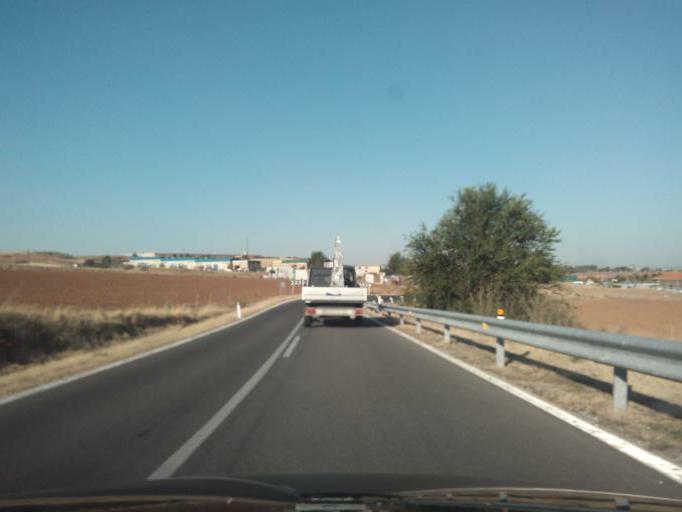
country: ES
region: Madrid
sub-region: Provincia de Madrid
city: Cobena
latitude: 40.5642
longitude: -3.4924
